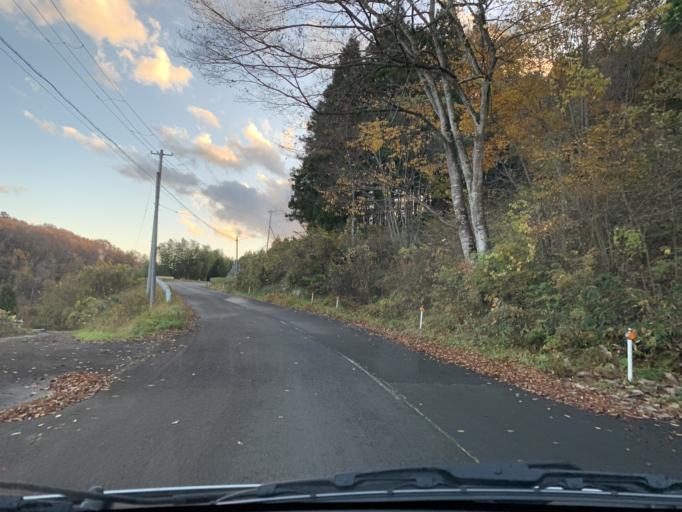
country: JP
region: Iwate
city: Mizusawa
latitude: 39.0277
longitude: 141.0363
